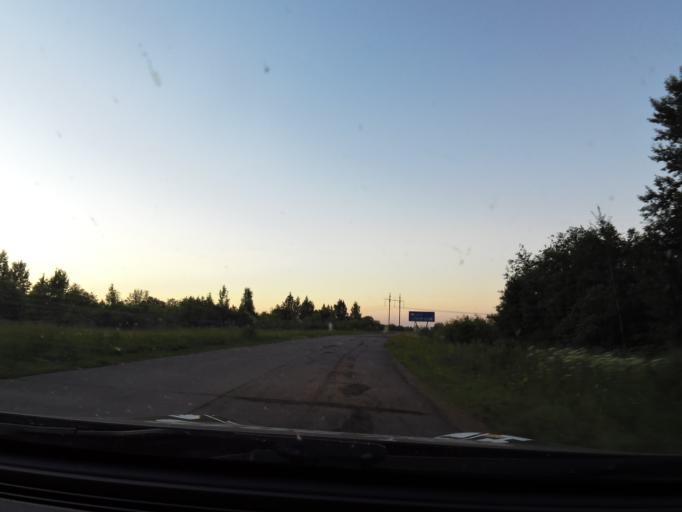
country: RU
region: Kostroma
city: Buy
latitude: 58.3956
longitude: 41.2263
